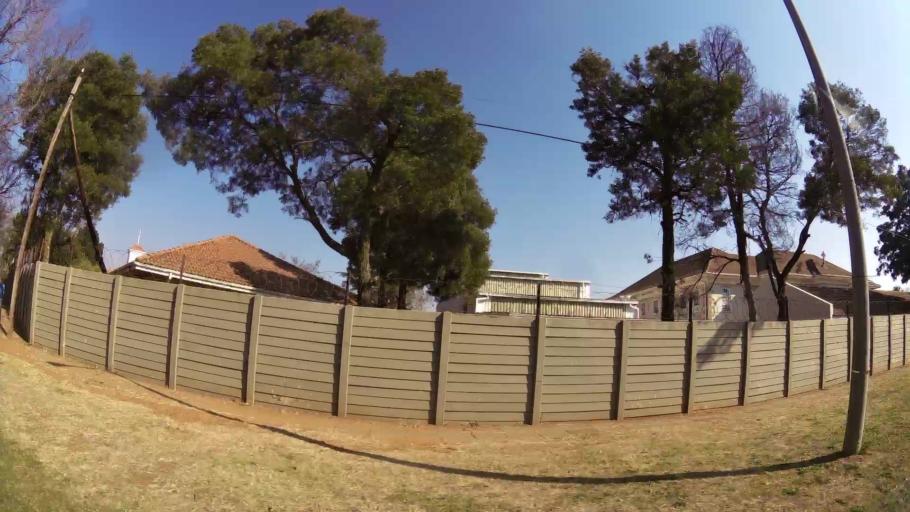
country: ZA
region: Gauteng
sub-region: Ekurhuleni Metropolitan Municipality
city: Boksburg
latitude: -26.2265
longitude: 28.2610
